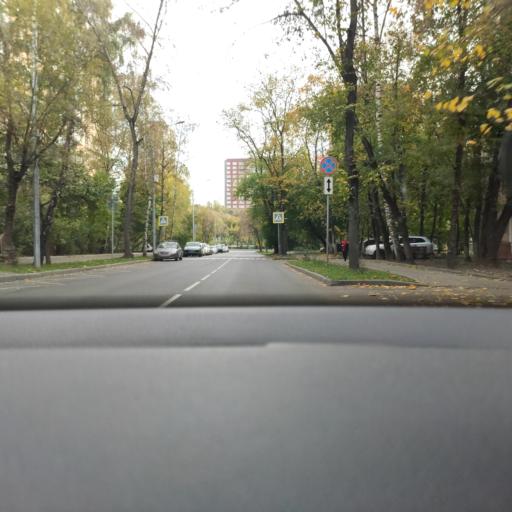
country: RU
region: Moskovskaya
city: Fili
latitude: 55.7391
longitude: 37.4707
